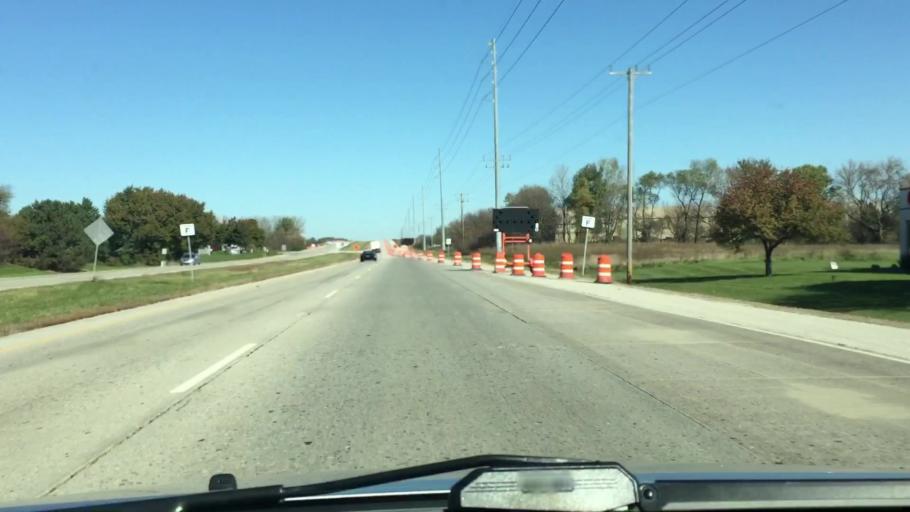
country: US
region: Wisconsin
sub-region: Waukesha County
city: Pewaukee
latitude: 43.0667
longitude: -88.2056
